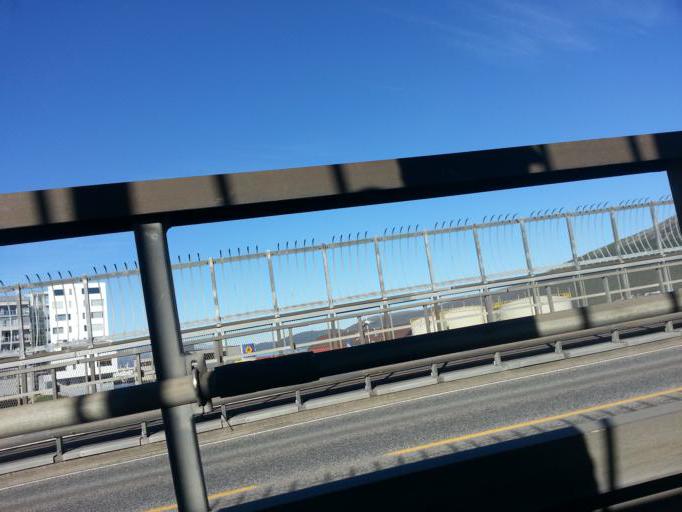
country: NO
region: Troms
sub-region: Tromso
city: Tromso
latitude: 69.6541
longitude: 18.9653
